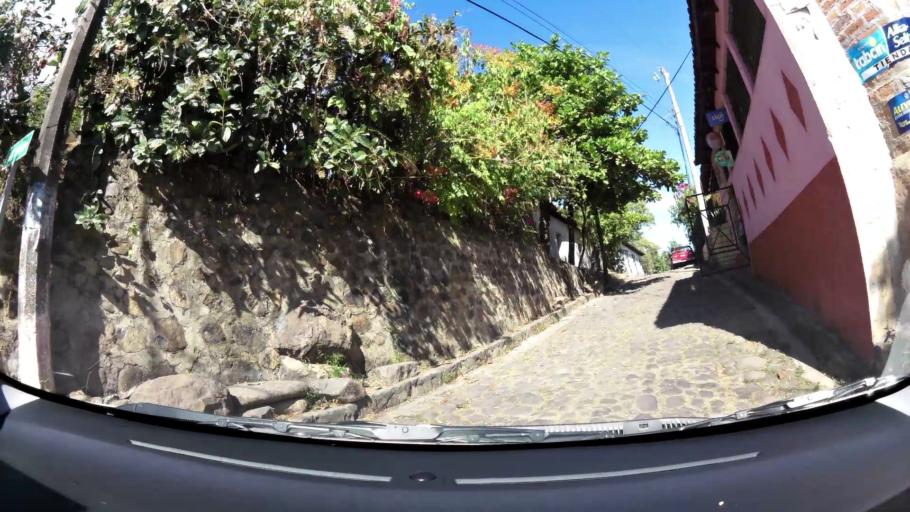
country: SV
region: Cuscatlan
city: Suchitoto
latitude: 13.9419
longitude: -89.0210
